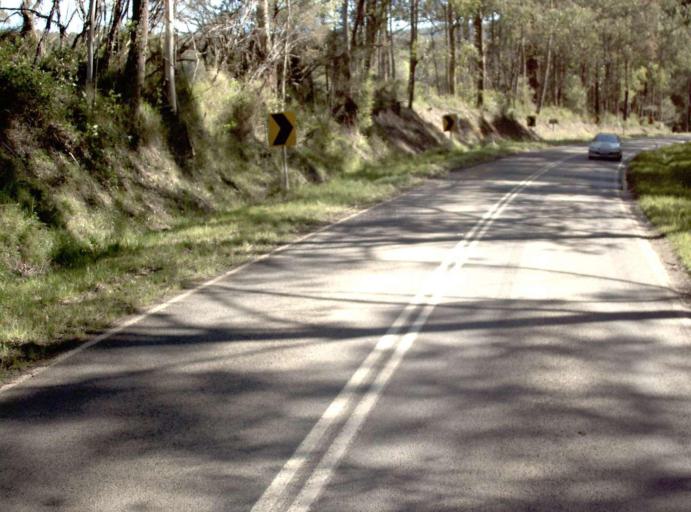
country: AU
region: Victoria
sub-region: Baw Baw
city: Warragul
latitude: -37.8933
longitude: 145.9255
